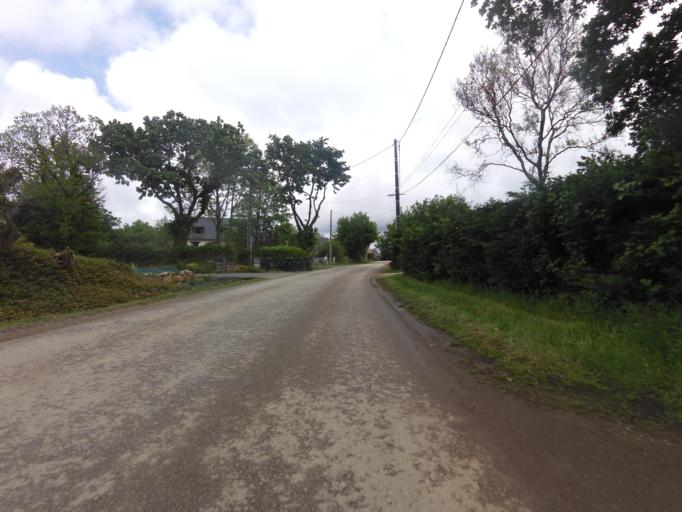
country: FR
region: Brittany
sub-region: Departement du Morbihan
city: Plougoumelen
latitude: 47.6413
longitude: -2.8988
